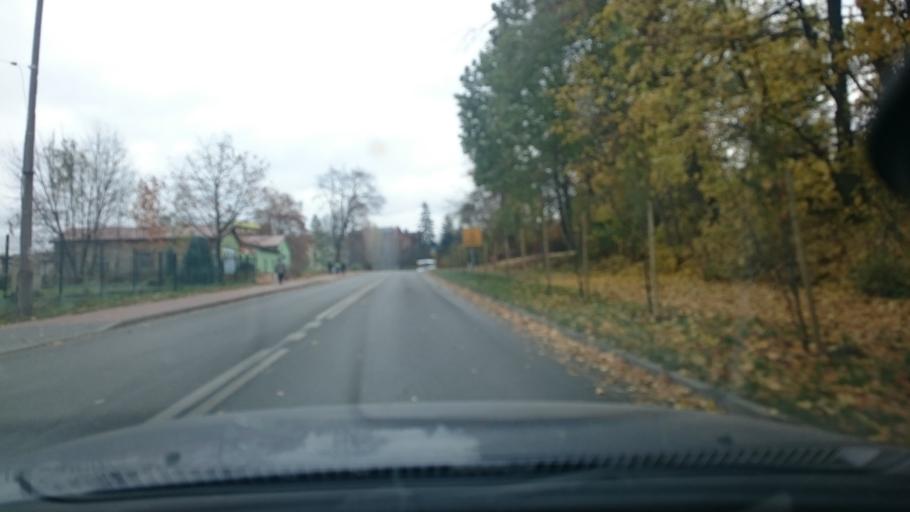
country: PL
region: Silesian Voivodeship
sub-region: Powiat bedzinski
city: Strzyzowice
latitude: 50.3534
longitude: 19.0756
